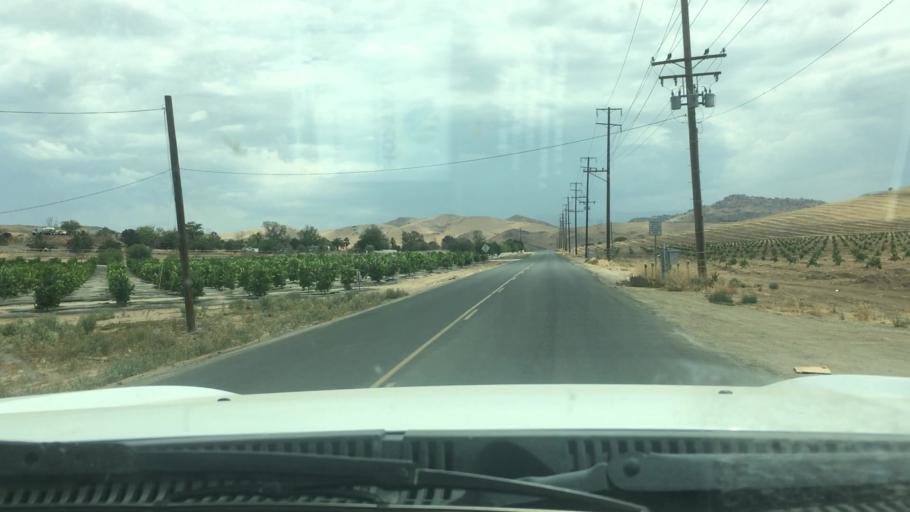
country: US
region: California
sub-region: Tulare County
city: Porterville
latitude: 36.0963
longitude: -119.0334
